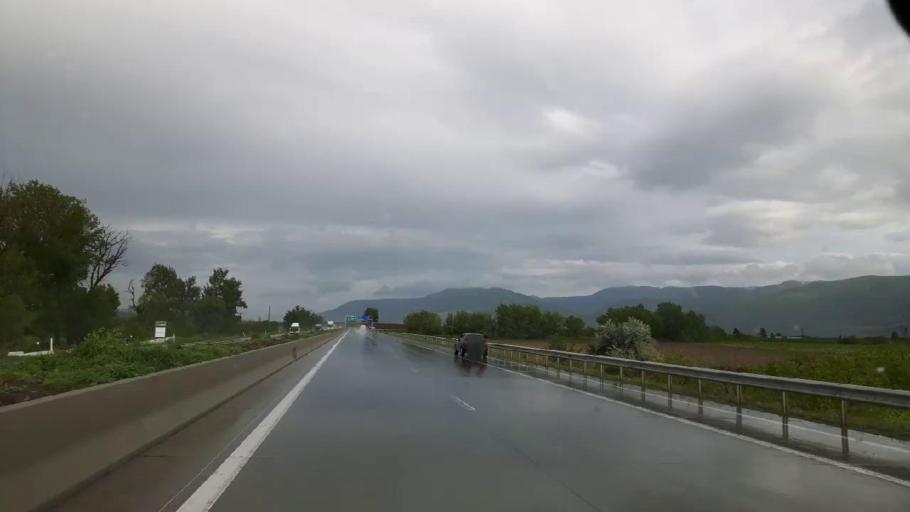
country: GE
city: Agara
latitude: 42.0350
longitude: 43.9415
